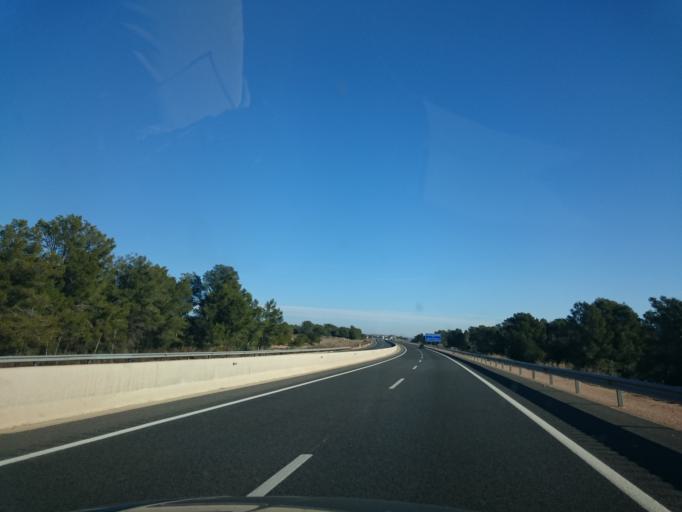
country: ES
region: Catalonia
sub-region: Provincia de Tarragona
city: Vilanova d'Escornalbou
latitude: 41.0420
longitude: 0.9634
